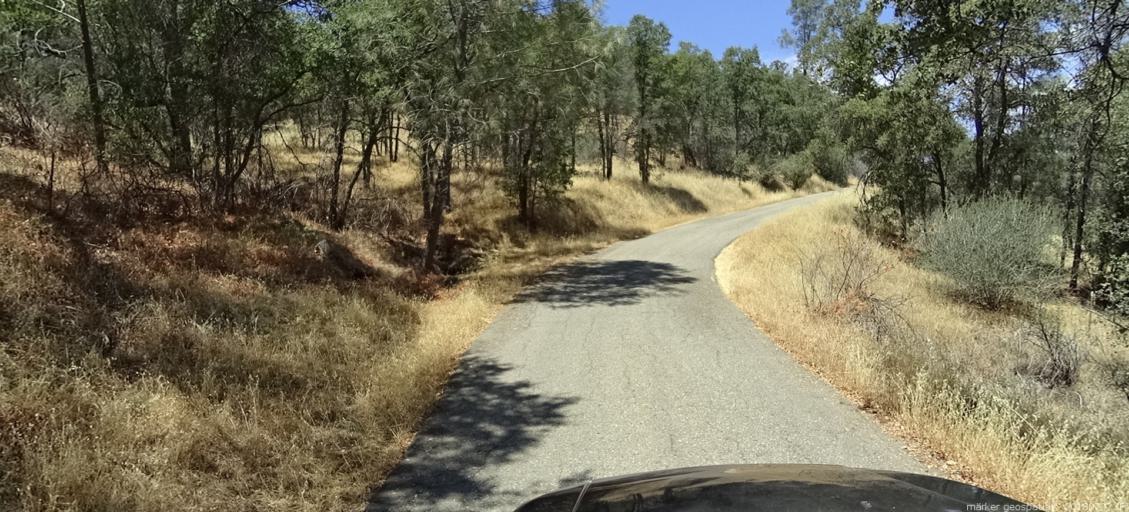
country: US
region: California
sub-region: Madera County
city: Coarsegold
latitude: 37.2504
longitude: -119.7338
